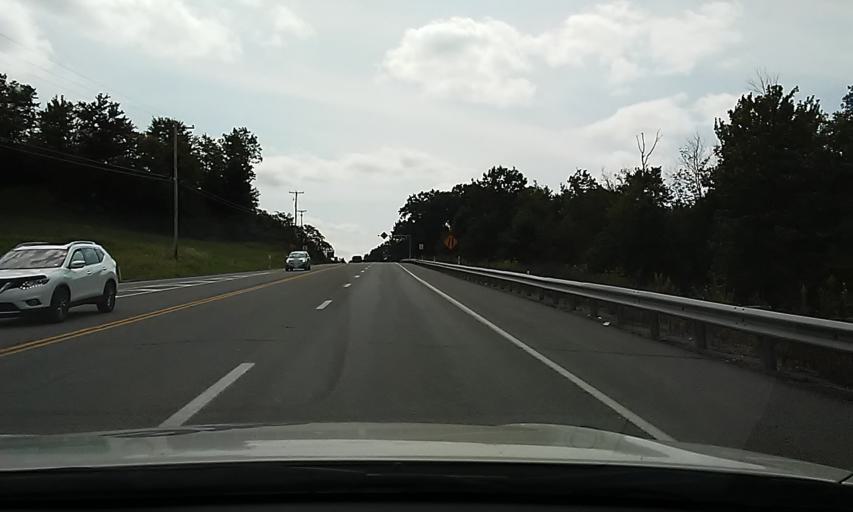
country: US
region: Pennsylvania
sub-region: Jefferson County
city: Punxsutawney
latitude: 40.9318
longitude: -78.9809
